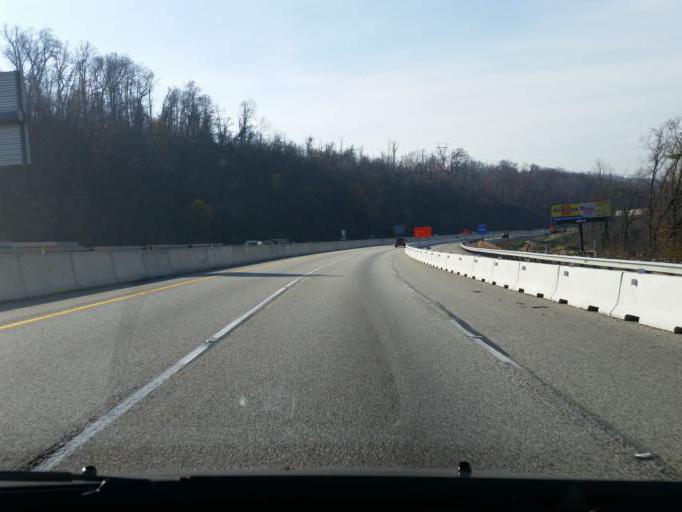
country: US
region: Pennsylvania
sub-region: Dauphin County
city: Highspire
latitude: 40.1995
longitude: -76.8101
